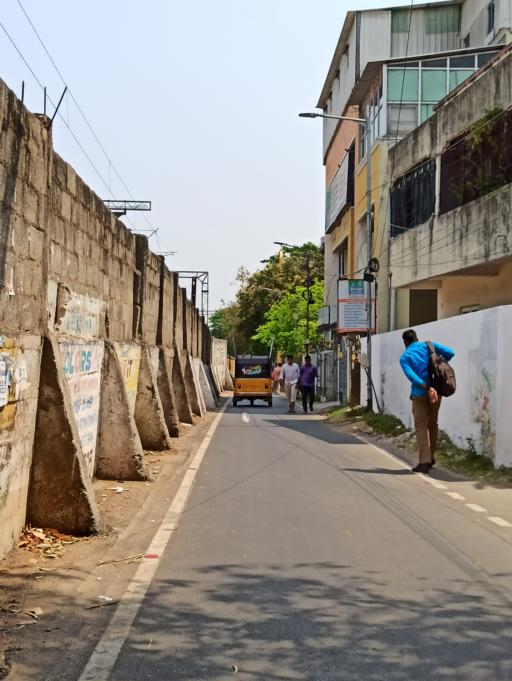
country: IN
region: Tamil Nadu
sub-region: Chennai
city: Chetput
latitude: 13.0637
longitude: 80.2323
